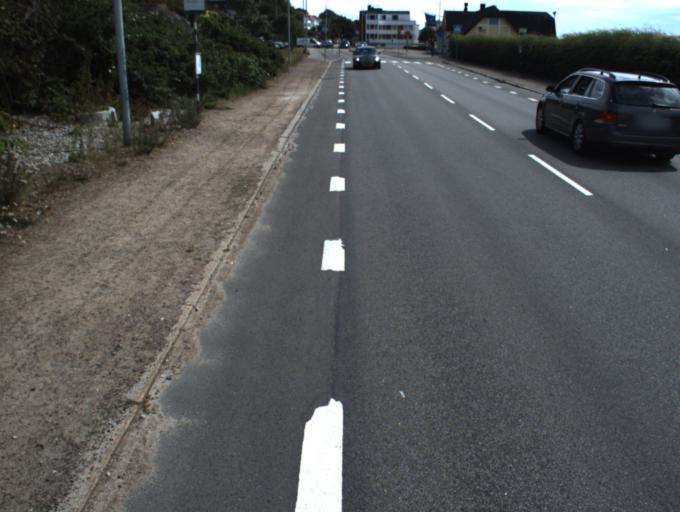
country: SE
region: Skane
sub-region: Helsingborg
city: Helsingborg
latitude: 56.0654
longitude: 12.6777
